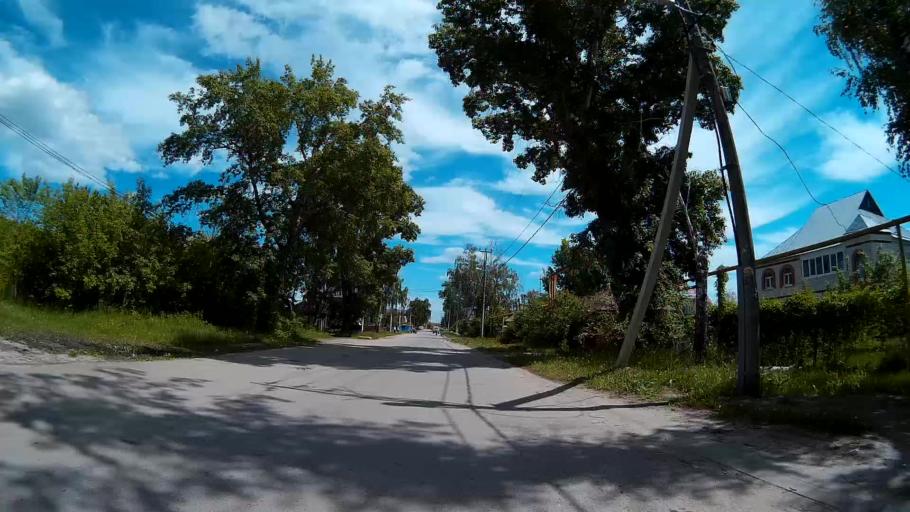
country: RU
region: Ulyanovsk
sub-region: Ulyanovskiy Rayon
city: Ulyanovsk
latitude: 54.2772
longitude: 48.3460
